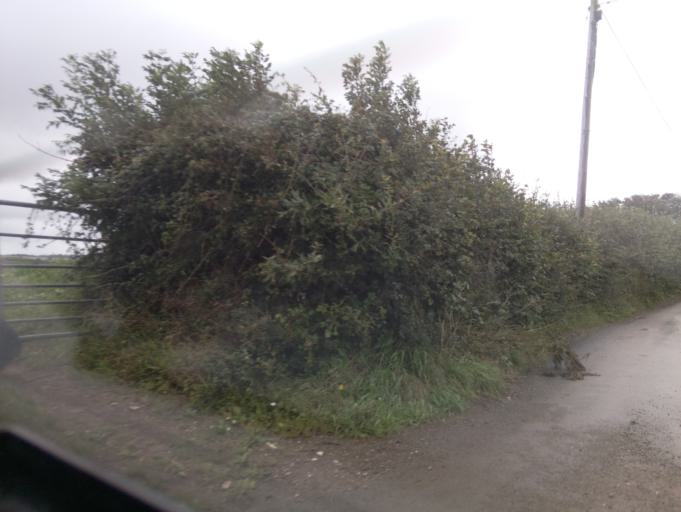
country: GB
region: England
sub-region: Devon
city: Totnes
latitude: 50.3289
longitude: -3.6828
